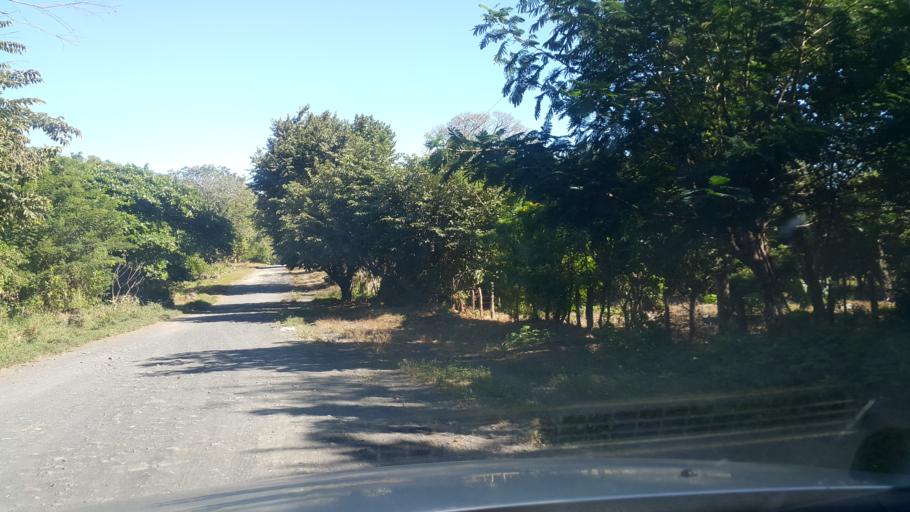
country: NI
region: Rivas
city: Altagracia
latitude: 11.4900
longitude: -85.6141
